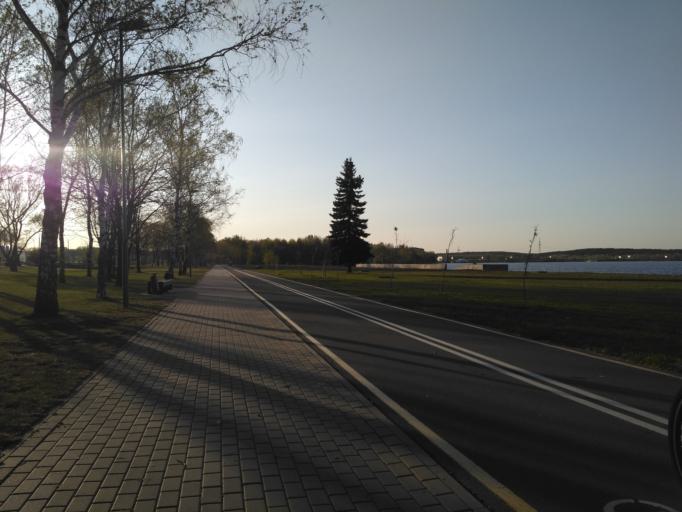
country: BY
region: Minsk
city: Zhdanovichy
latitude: 53.9442
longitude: 27.4631
